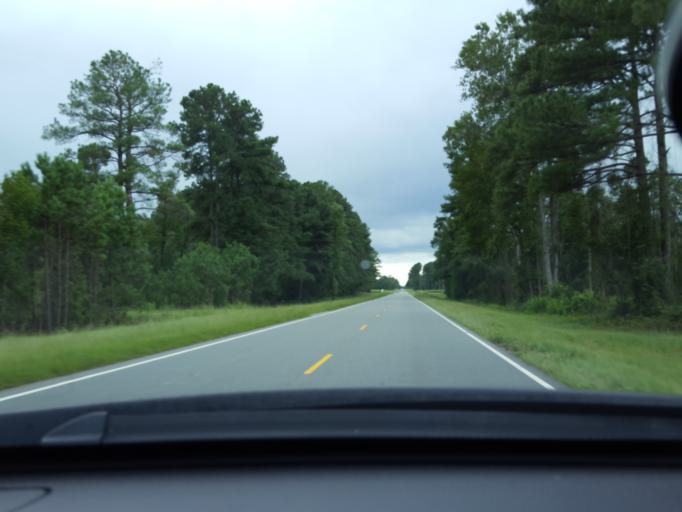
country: US
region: North Carolina
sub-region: Bladen County
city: Elizabethtown
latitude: 34.7432
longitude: -78.4261
